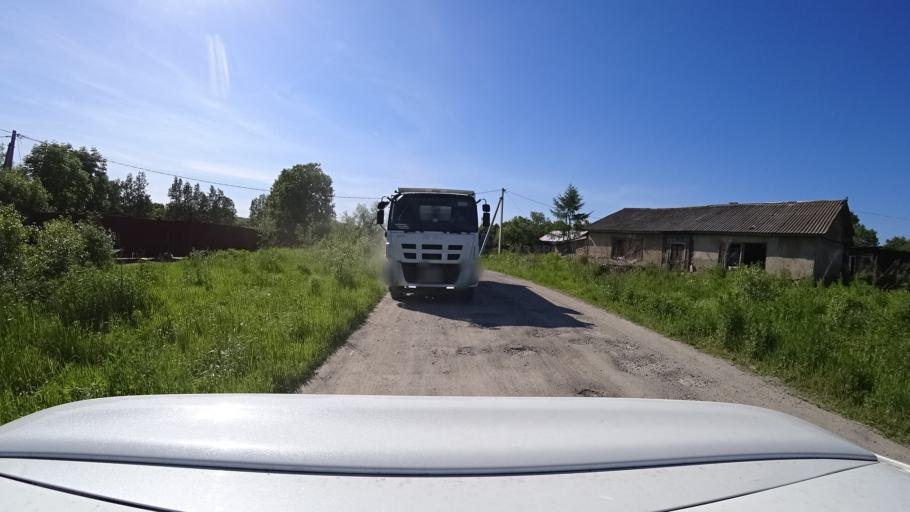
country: RU
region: Khabarovsk Krai
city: Topolevo
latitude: 48.5514
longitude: 135.1894
